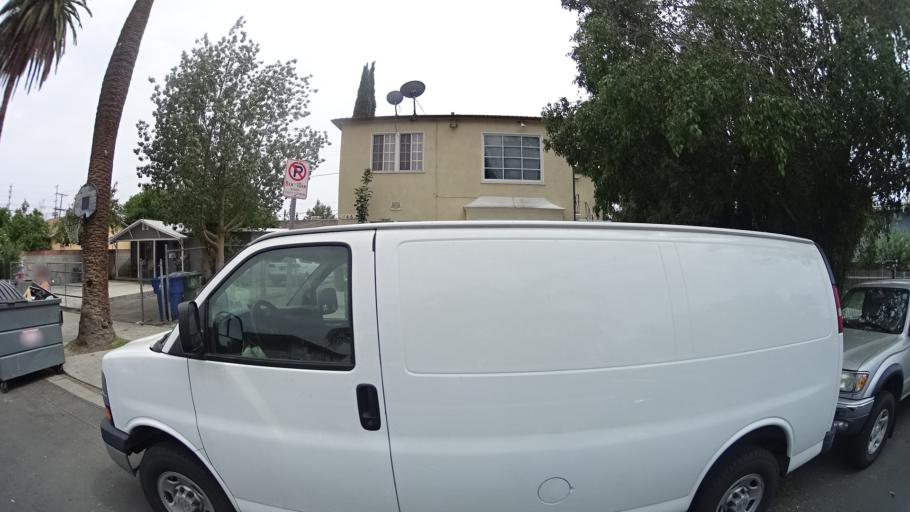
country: US
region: California
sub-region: Los Angeles County
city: Van Nuys
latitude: 34.1817
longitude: -118.4521
